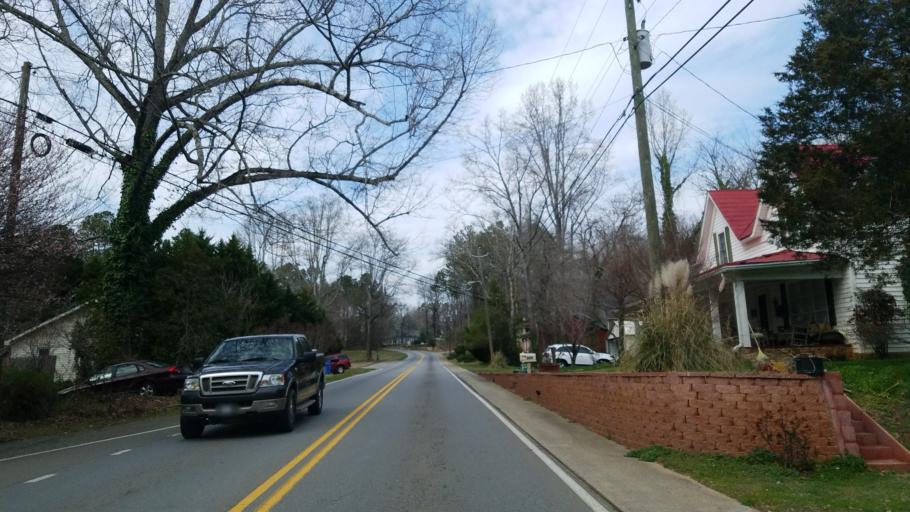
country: US
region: Georgia
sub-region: Cherokee County
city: Ball Ground
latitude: 34.3322
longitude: -84.3703
